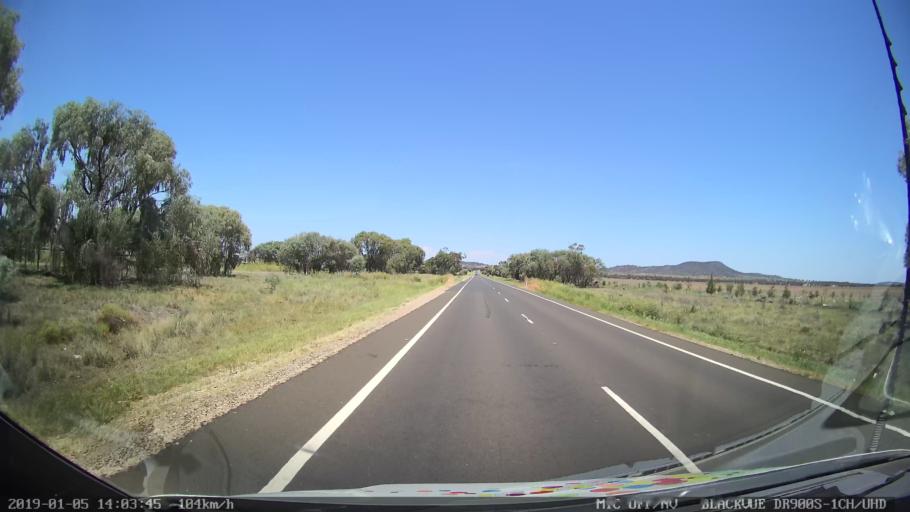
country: AU
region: New South Wales
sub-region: Gunnedah
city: Gunnedah
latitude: -31.1929
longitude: 150.3548
